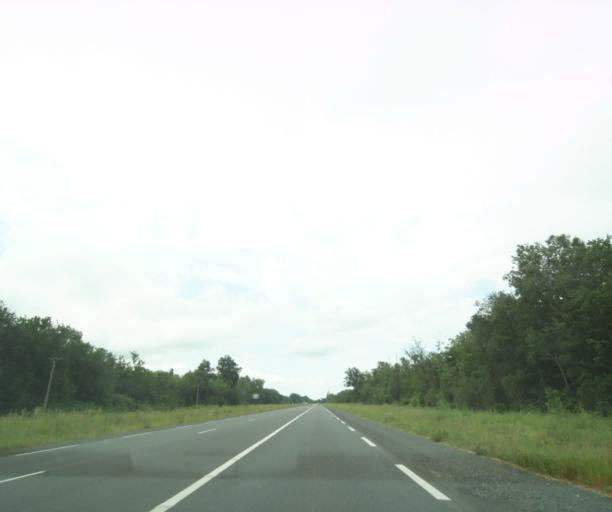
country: FR
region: Pays de la Loire
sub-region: Departement de Maine-et-Loire
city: Montreuil-Bellay
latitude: 47.0745
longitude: -0.1771
